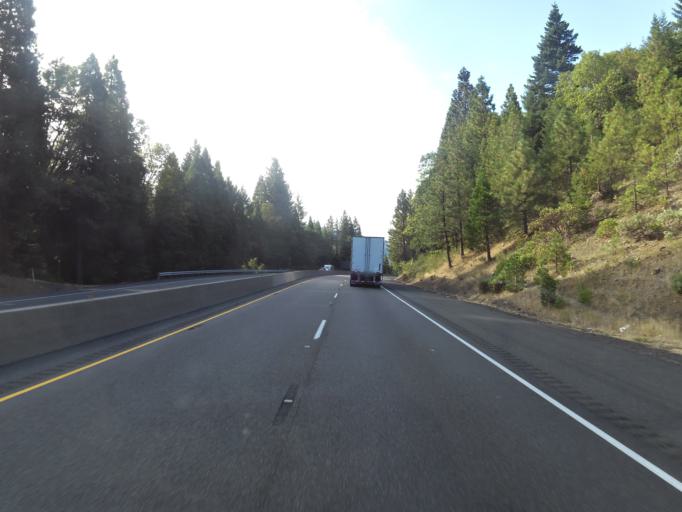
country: US
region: California
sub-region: Siskiyou County
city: Dunsmuir
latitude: 41.2025
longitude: -122.2777
